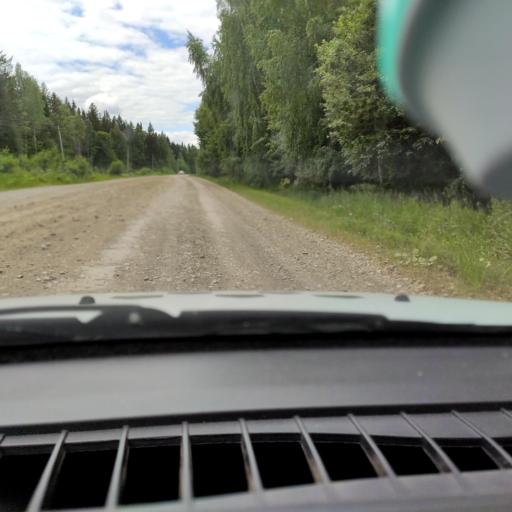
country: RU
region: Perm
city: Suksun
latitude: 57.1343
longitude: 57.5033
